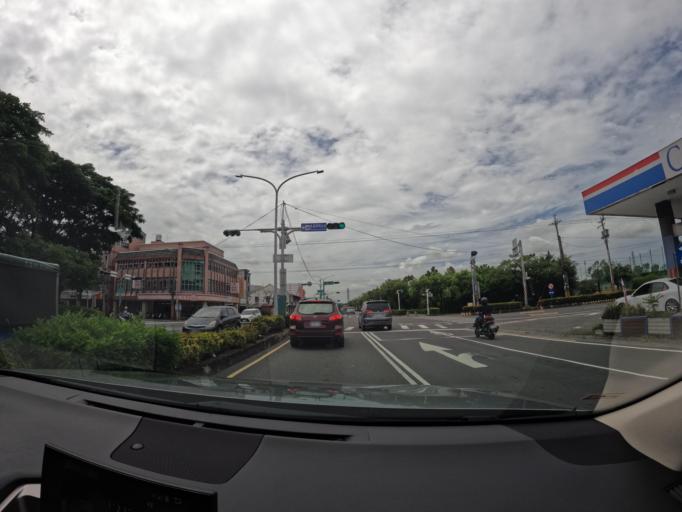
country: TW
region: Kaohsiung
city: Kaohsiung
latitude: 22.7825
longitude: 120.2978
